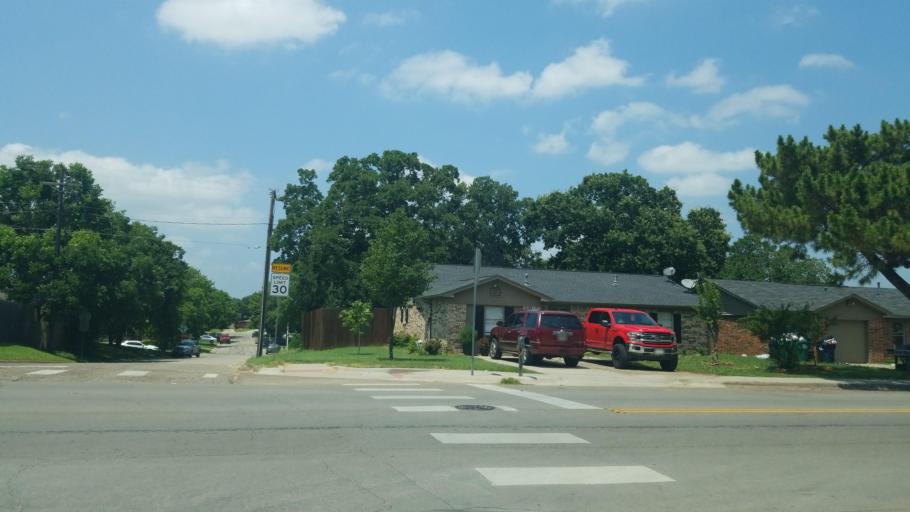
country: US
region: Texas
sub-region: Denton County
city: Denton
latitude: 33.2207
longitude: -97.1059
